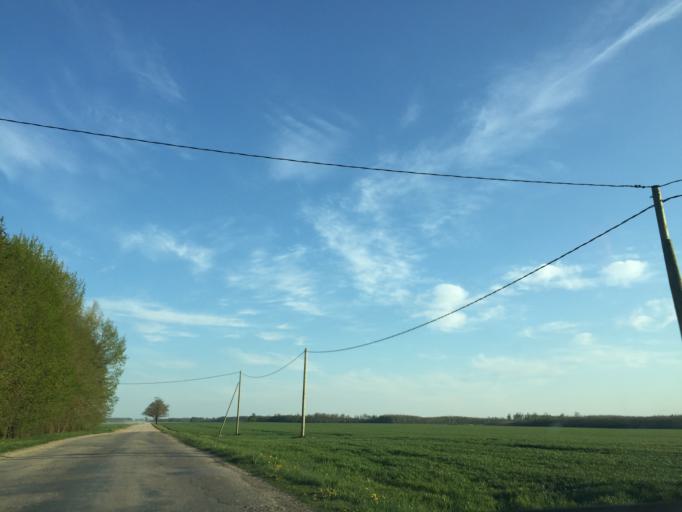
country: LV
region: Bauskas Rajons
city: Bauska
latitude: 56.2952
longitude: 24.2614
